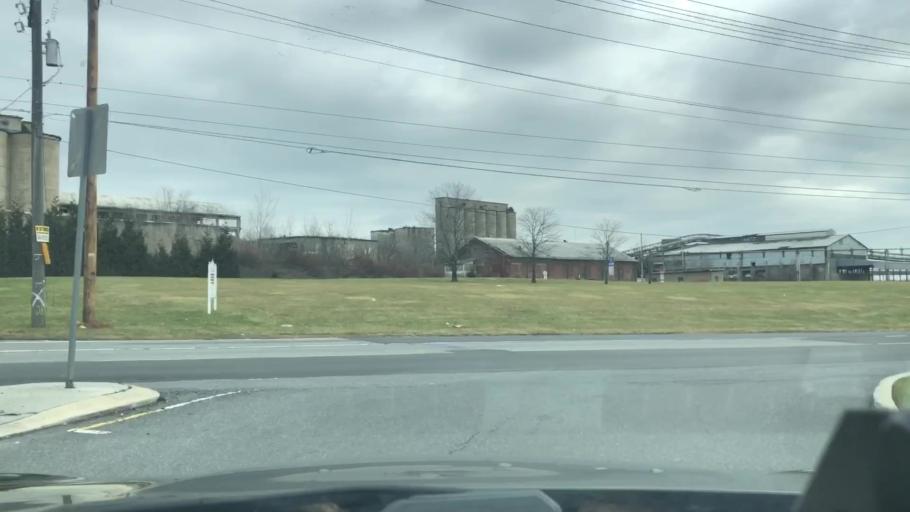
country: US
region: Pennsylvania
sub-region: Northampton County
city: Nazareth
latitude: 40.7316
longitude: -75.3064
